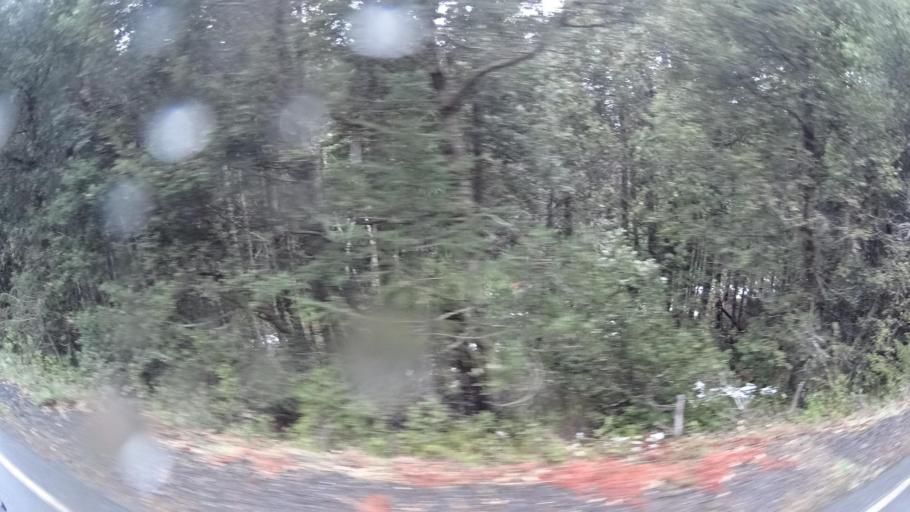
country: US
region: California
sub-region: Humboldt County
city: Willow Creek
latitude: 41.1705
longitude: -123.8137
